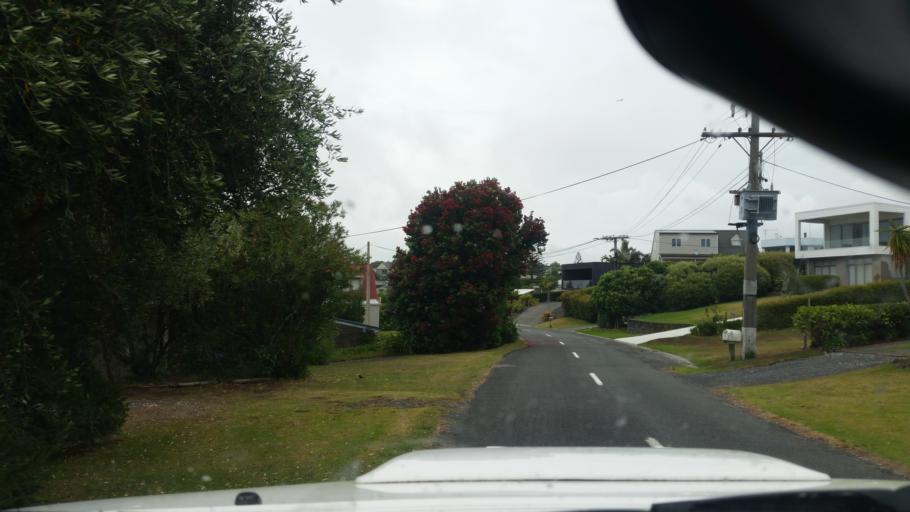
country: NZ
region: Auckland
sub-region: Auckland
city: Wellsford
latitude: -36.0979
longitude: 174.5889
